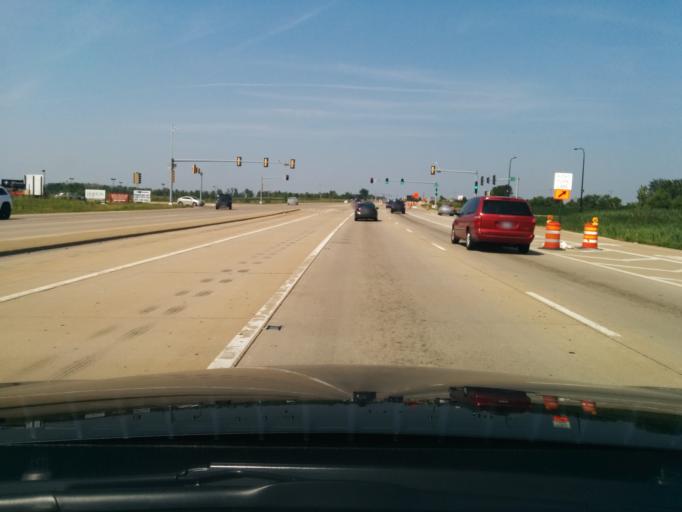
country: US
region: Illinois
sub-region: Cook County
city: Orland Hills
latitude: 41.5594
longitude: -87.8532
